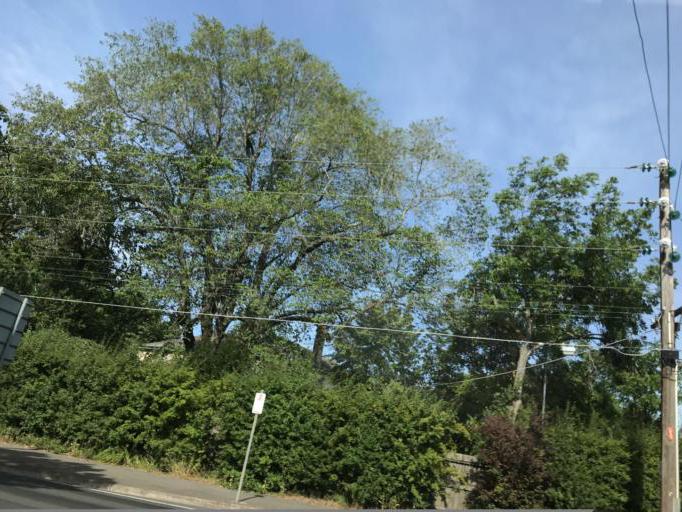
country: AU
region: Victoria
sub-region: Ballarat North
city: Newington
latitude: -37.5546
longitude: 143.8193
